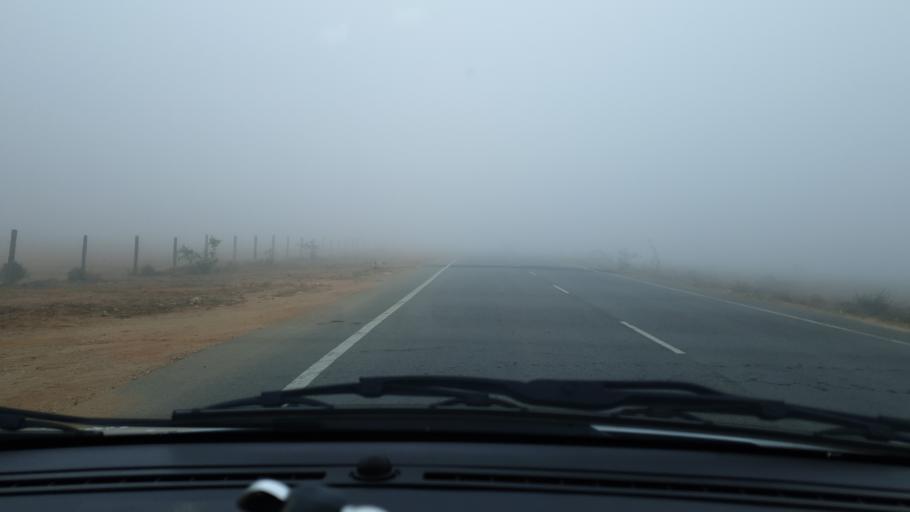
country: IN
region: Telangana
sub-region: Mahbubnagar
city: Nagar Karnul
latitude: 16.6829
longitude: 78.5253
